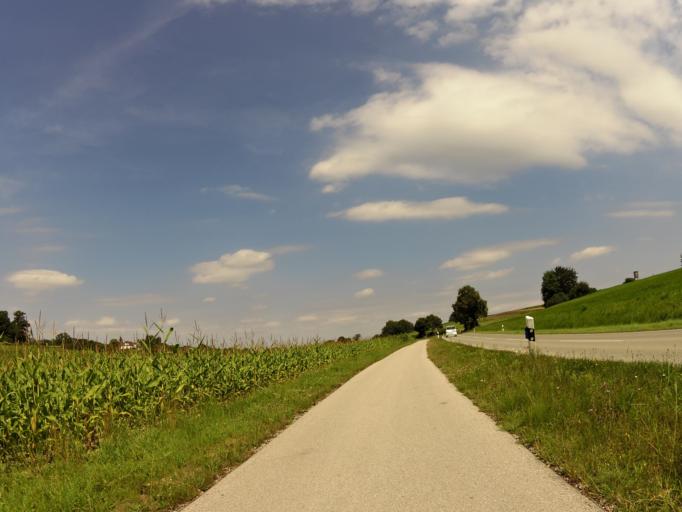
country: DE
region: Bavaria
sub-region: Upper Bavaria
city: Inning am Ammersee
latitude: 48.0629
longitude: 11.1434
